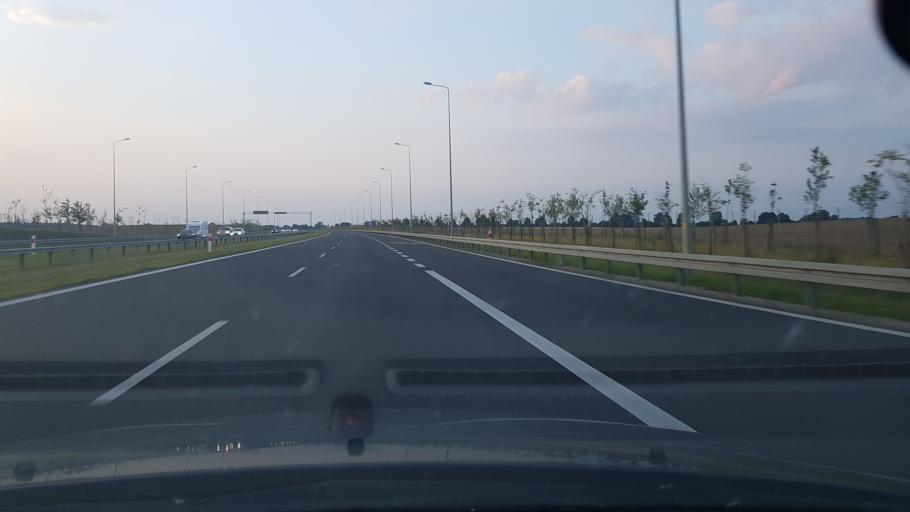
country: PL
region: Warmian-Masurian Voivodeship
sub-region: Powiat nidzicki
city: Nidzica
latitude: 53.2782
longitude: 20.4377
